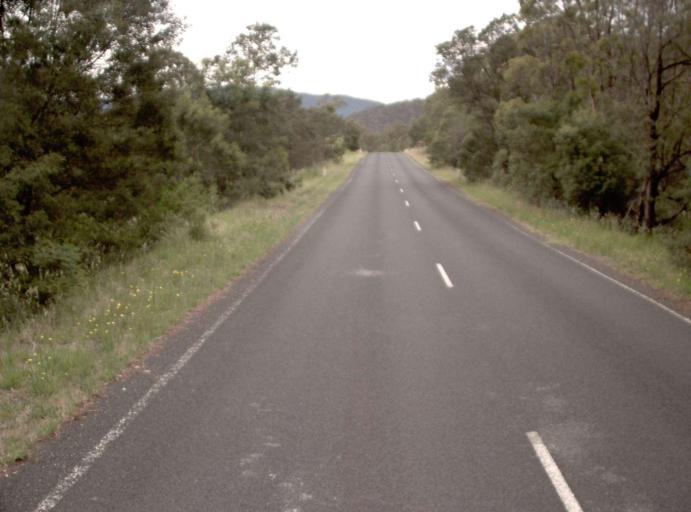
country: AU
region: Victoria
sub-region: East Gippsland
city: Bairnsdale
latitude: -37.5620
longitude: 147.1926
